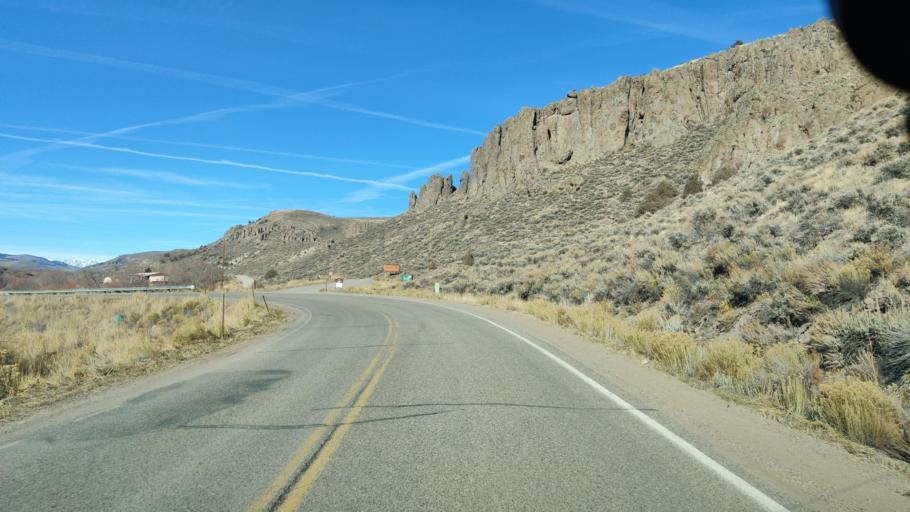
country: US
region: Colorado
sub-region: Gunnison County
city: Gunnison
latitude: 38.5769
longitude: -106.9618
